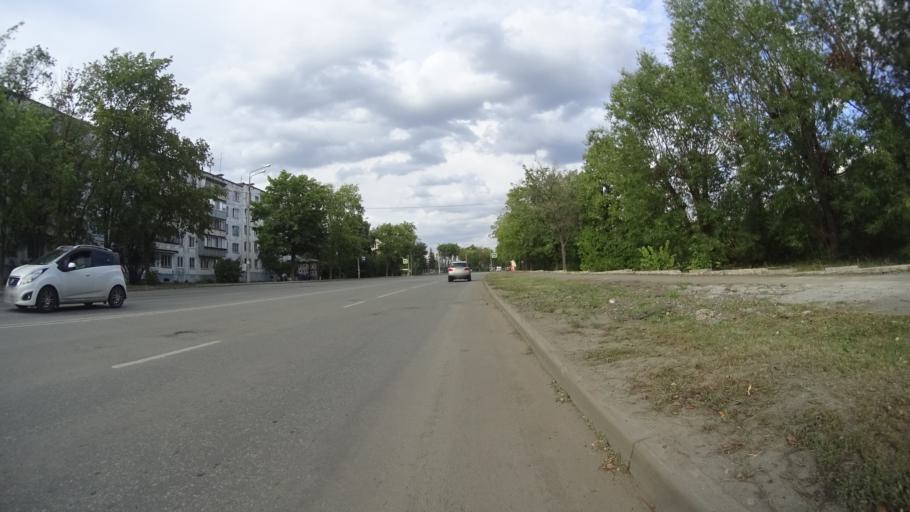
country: RU
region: Chelyabinsk
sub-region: Gorod Chelyabinsk
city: Chelyabinsk
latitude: 55.2015
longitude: 61.3206
